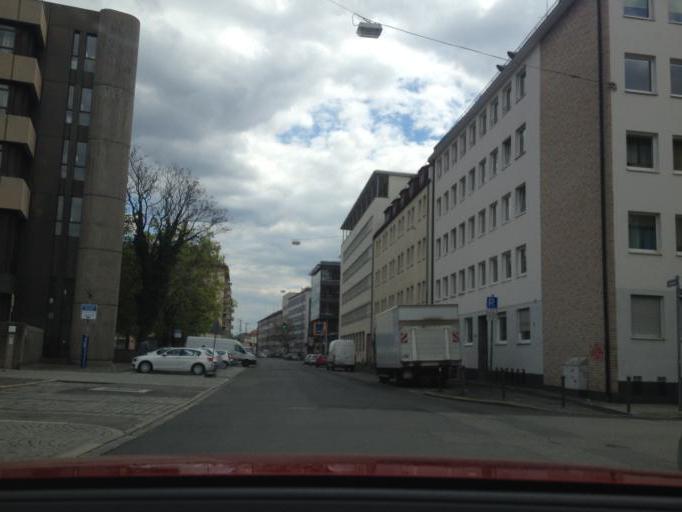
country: DE
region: Bavaria
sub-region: Regierungsbezirk Mittelfranken
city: Nuernberg
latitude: 49.4463
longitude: 11.0700
